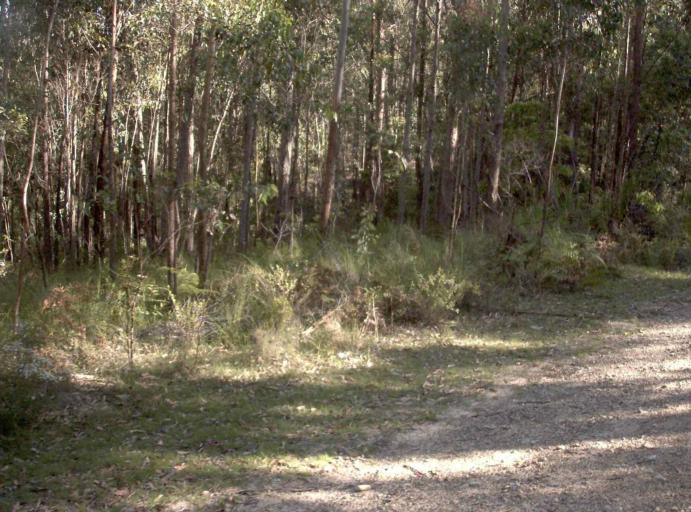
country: AU
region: Victoria
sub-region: East Gippsland
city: Lakes Entrance
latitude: -37.6319
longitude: 148.4871
